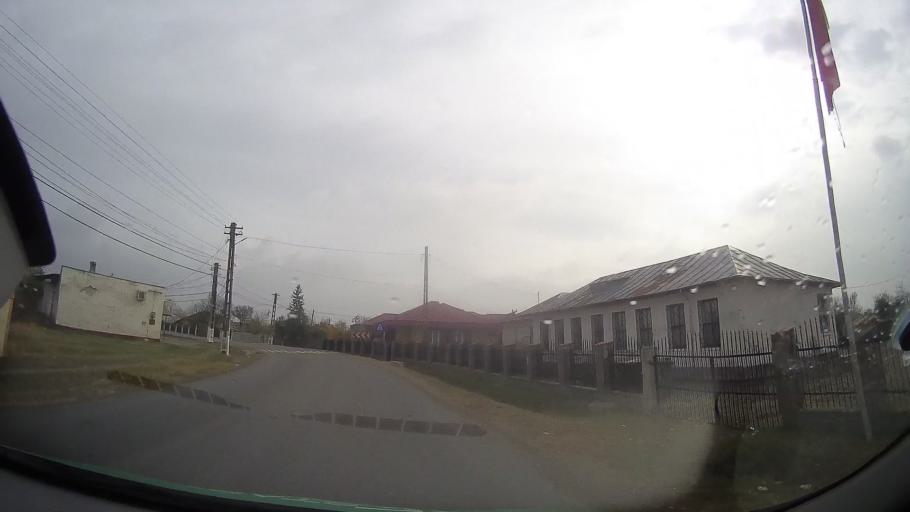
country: RO
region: Prahova
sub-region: Comuna Rafov
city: Palanca
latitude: 44.8415
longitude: 26.2381
